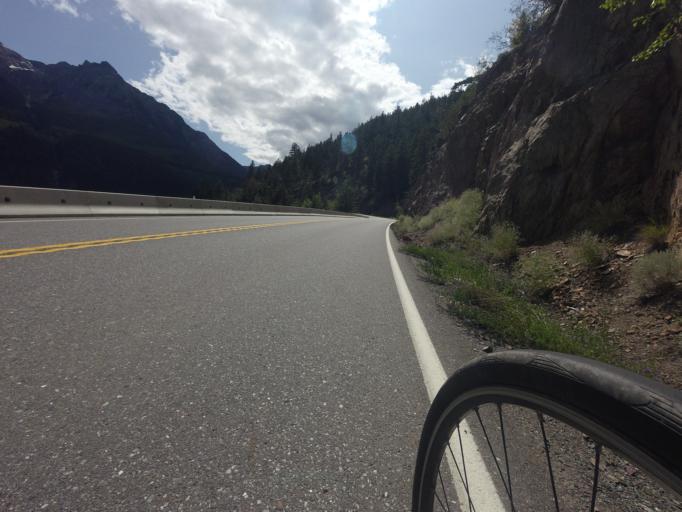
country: CA
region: British Columbia
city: Lillooet
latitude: 50.6558
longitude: -122.0000
